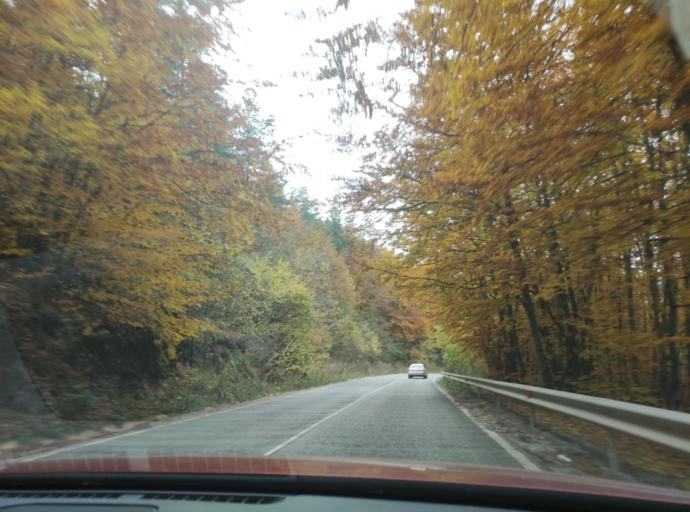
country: BG
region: Sofiya
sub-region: Obshtina Godech
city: Godech
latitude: 43.0262
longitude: 23.1366
